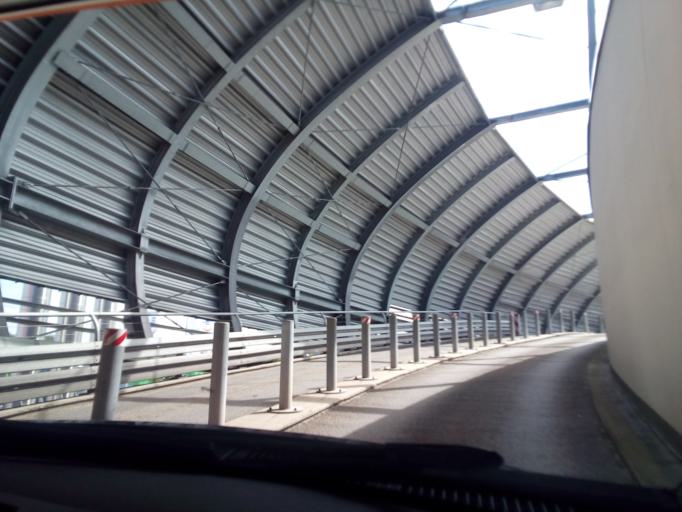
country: DE
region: Baden-Wuerttemberg
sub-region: Karlsruhe Region
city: Sinzheim
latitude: 48.7834
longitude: 8.1929
